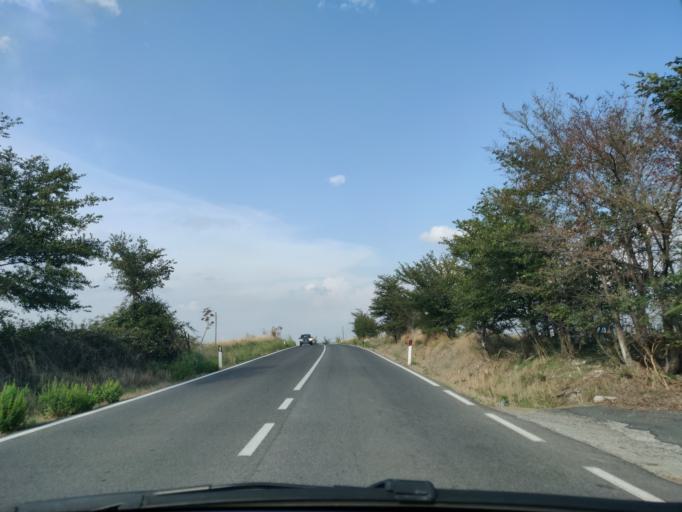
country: IT
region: Latium
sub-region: Provincia di Viterbo
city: Tarquinia
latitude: 42.2442
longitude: 11.8081
